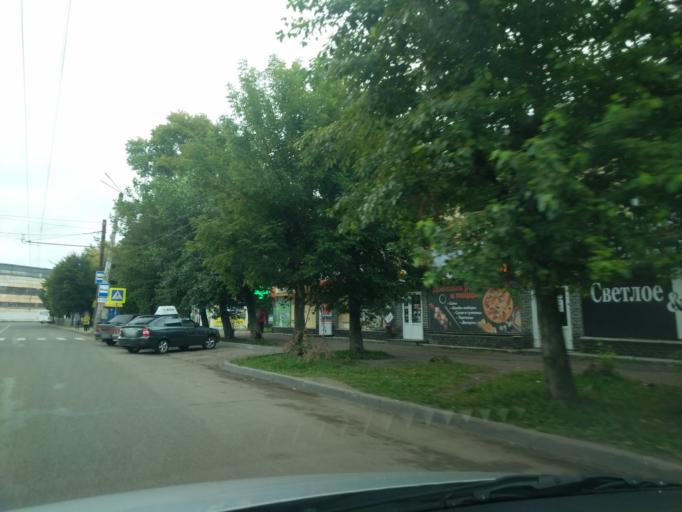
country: RU
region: Kirov
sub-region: Kirovo-Chepetskiy Rayon
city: Kirov
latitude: 58.6374
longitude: 49.6237
